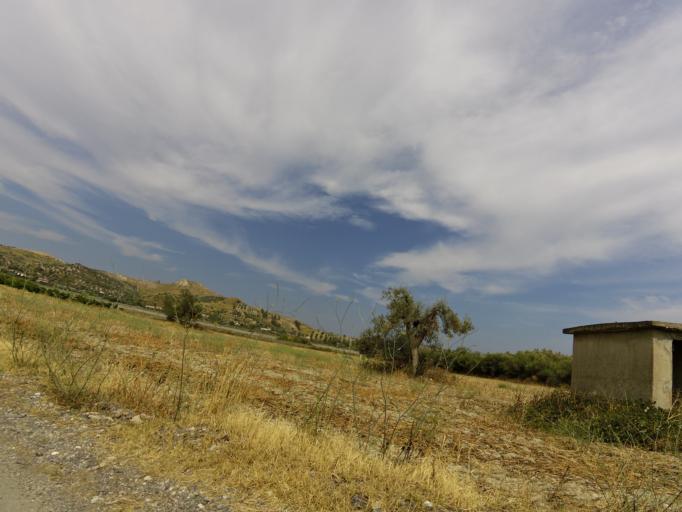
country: IT
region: Calabria
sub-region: Provincia di Reggio Calabria
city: Monasterace
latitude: 38.4487
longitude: 16.5213
